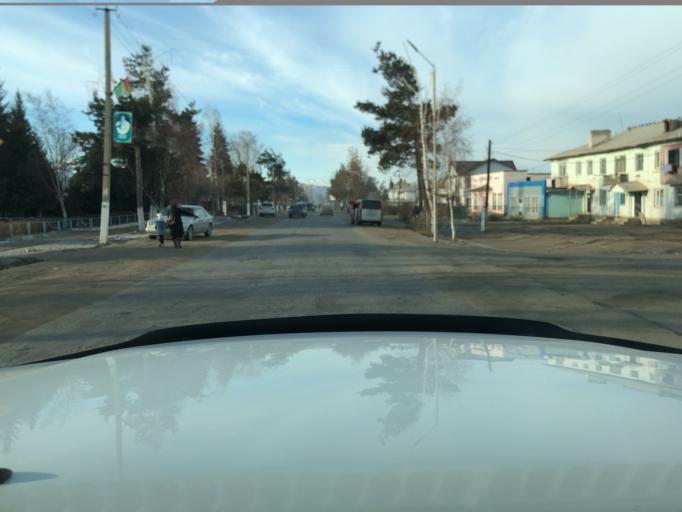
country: KG
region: Ysyk-Koel
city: Pokrovka
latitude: 42.3425
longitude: 78.0057
